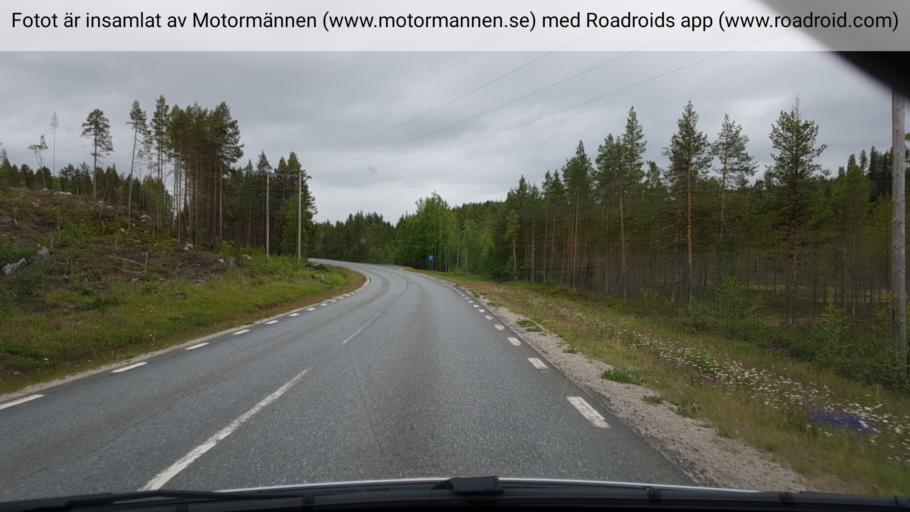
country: SE
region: Vaesterbotten
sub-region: Lycksele Kommun
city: Lycksele
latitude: 64.4686
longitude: 18.8992
